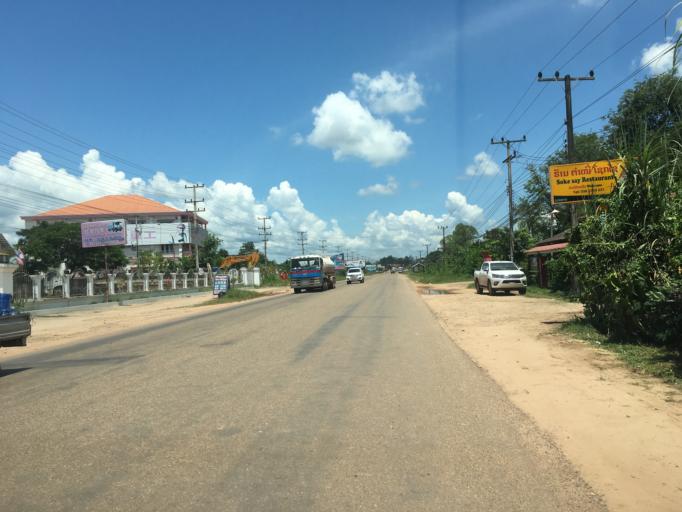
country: LA
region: Vientiane
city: Vientiane
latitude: 18.0521
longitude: 102.5438
